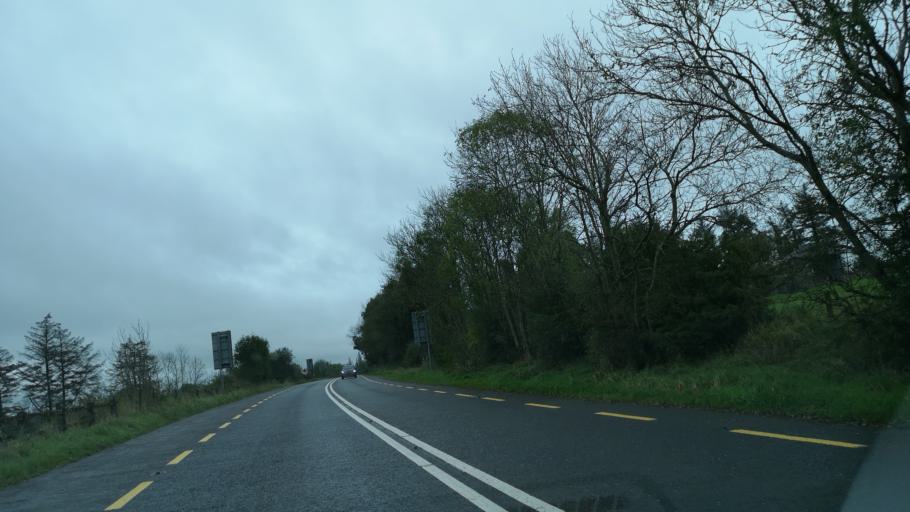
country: IE
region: Connaught
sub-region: Roscommon
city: Ballaghaderreen
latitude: 53.8958
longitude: -8.5622
